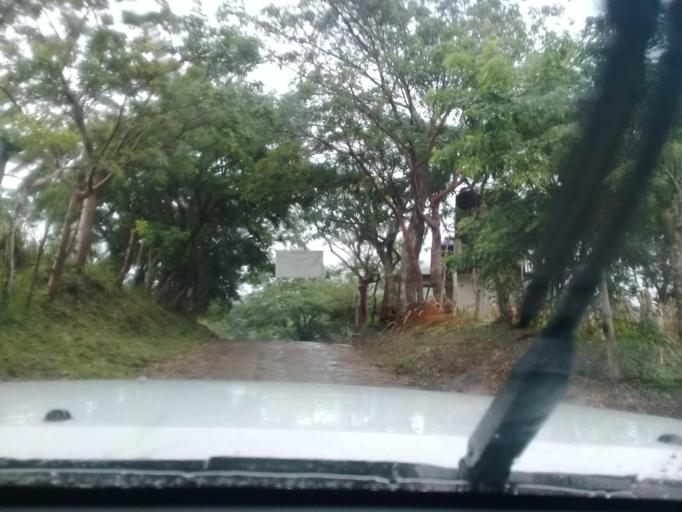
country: MX
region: Veracruz
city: Santiago Tuxtla
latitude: 18.4462
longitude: -95.2912
